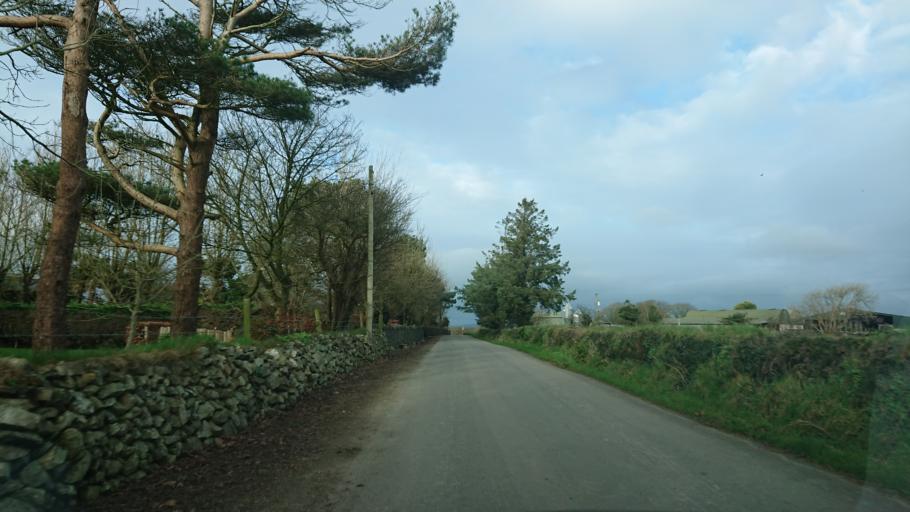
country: IE
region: Munster
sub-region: Waterford
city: Tra Mhor
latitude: 52.1489
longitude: -7.2112
